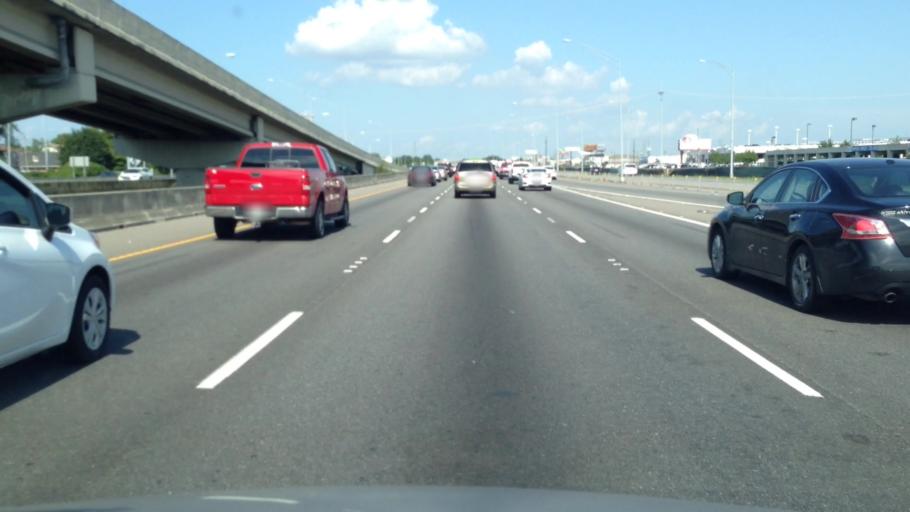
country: US
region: Louisiana
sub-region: Jefferson Parish
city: Kenner
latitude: 30.0097
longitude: -90.2371
